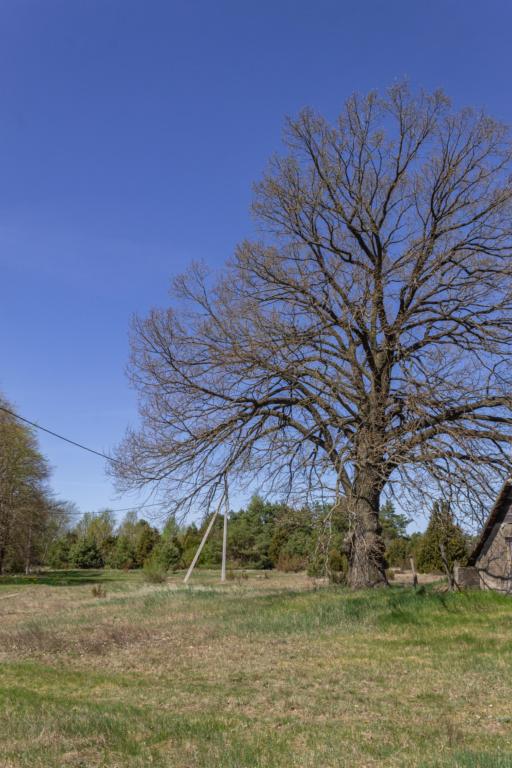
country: BY
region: Brest
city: Kamyanyets
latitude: 52.4198
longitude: 23.8364
